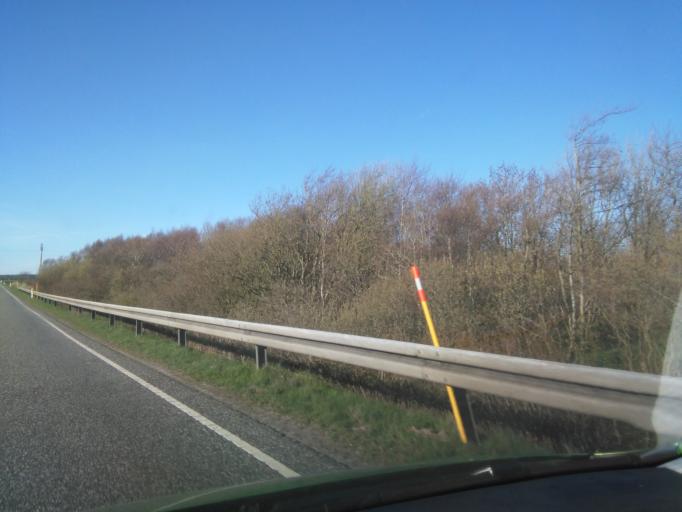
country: DK
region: Central Jutland
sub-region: Ringkobing-Skjern Kommune
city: Skjern
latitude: 56.0657
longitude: 8.5054
